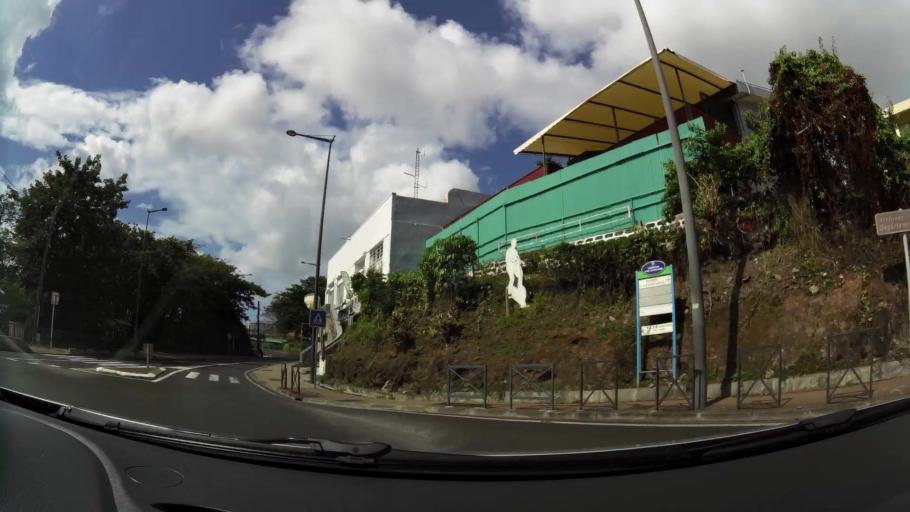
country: MQ
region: Martinique
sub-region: Martinique
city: Fort-de-France
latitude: 14.6031
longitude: -61.0787
